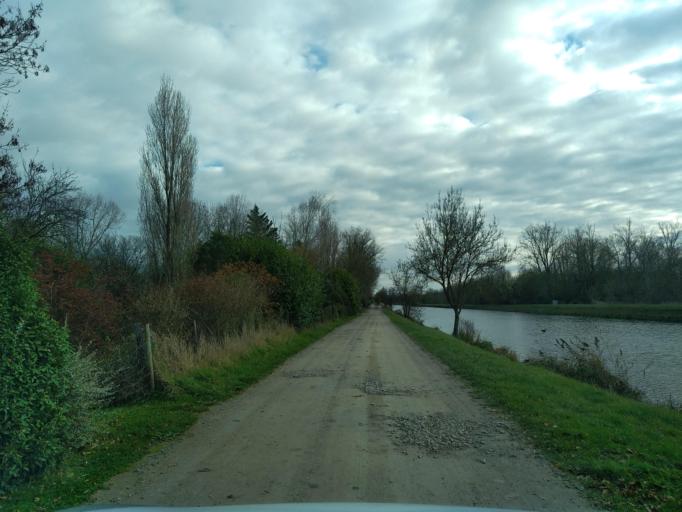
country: FR
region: Pays de la Loire
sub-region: Departement de la Vendee
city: Maillezais
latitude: 46.3131
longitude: -0.7703
